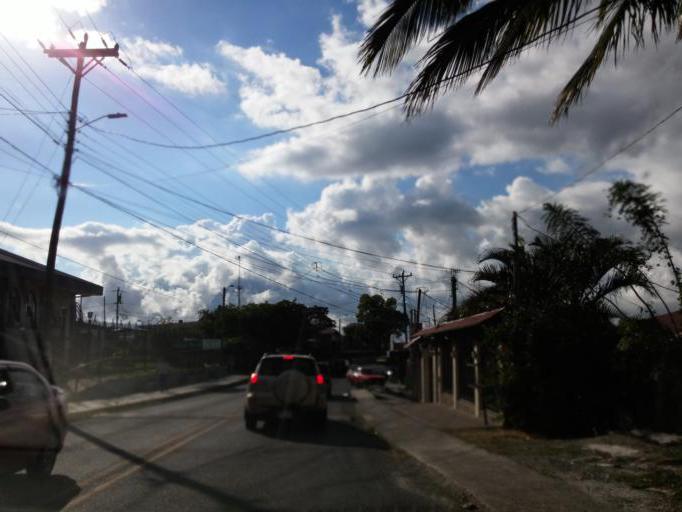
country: CR
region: San Jose
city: San Ignacio
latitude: 9.7966
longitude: -84.1291
